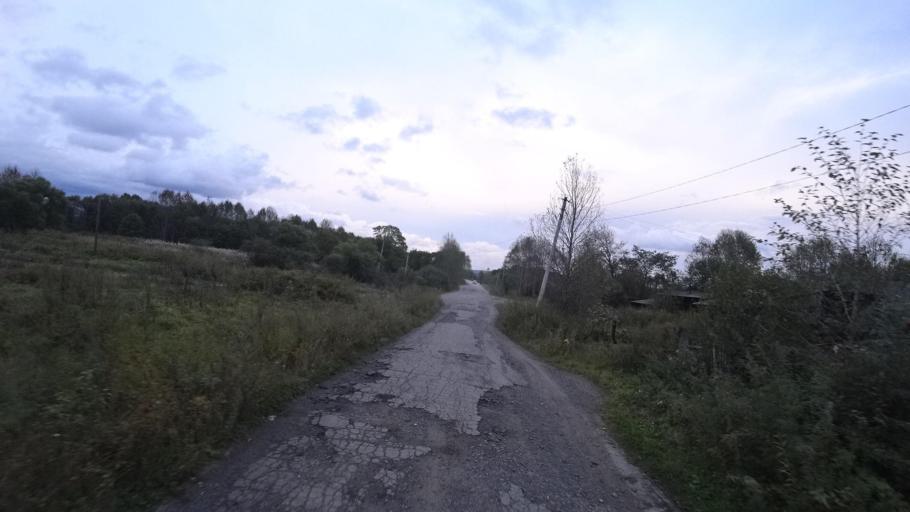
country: RU
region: Jewish Autonomous Oblast
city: Izvestkovyy
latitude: 48.9893
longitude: 131.5531
